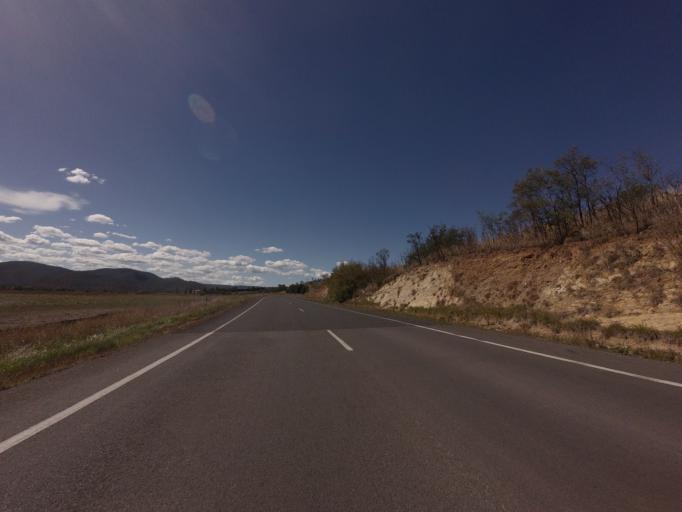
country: AU
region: Tasmania
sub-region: Break O'Day
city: St Helens
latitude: -41.7331
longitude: 147.8189
